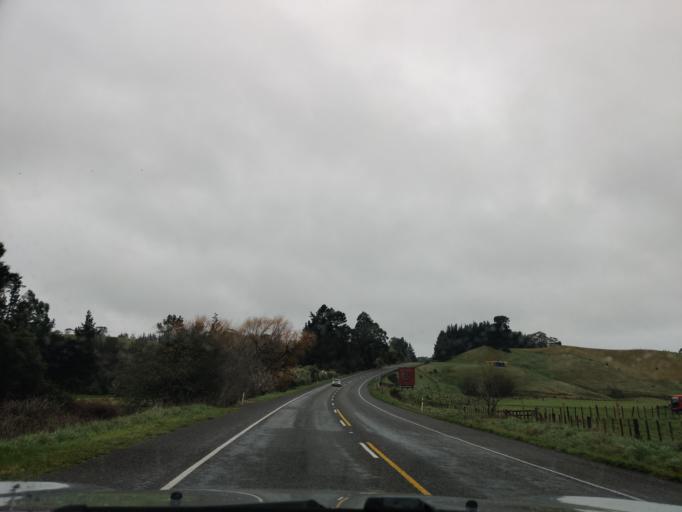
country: NZ
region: Manawatu-Wanganui
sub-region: Palmerston North City
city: Palmerston North
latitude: -40.0794
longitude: 176.2071
